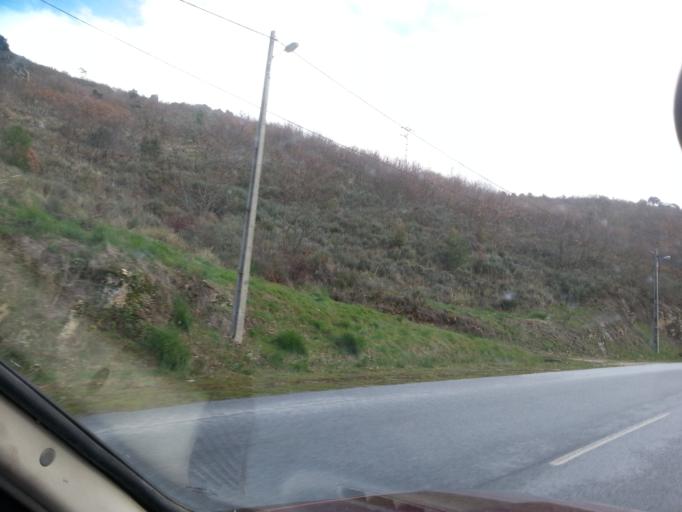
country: PT
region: Guarda
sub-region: Guarda
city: Guarda
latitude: 40.5670
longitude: -7.2982
